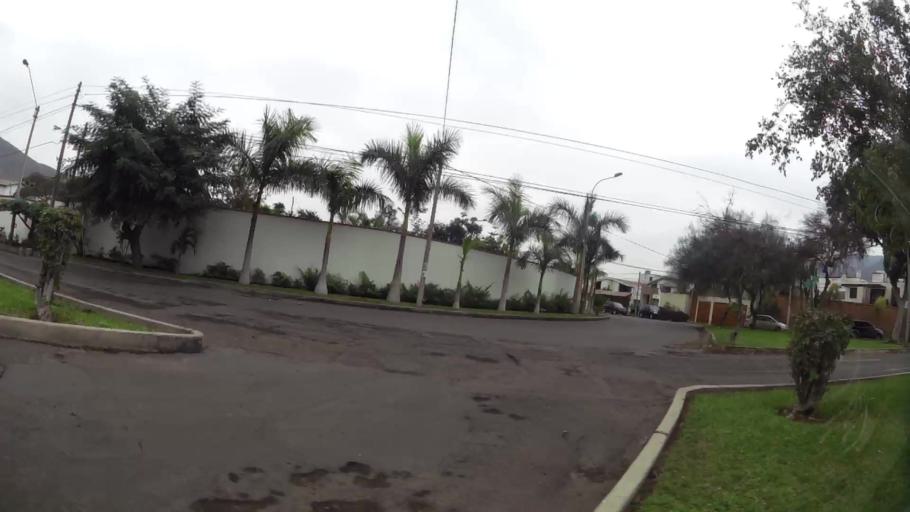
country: PE
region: Lima
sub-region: Lima
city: La Molina
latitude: -12.0868
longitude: -76.9208
